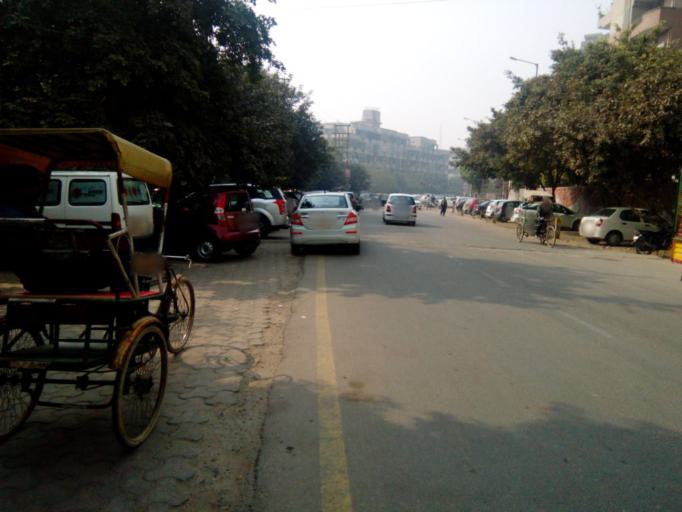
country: IN
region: Uttar Pradesh
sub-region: Gautam Buddha Nagar
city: Noida
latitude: 28.6348
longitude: 77.3652
